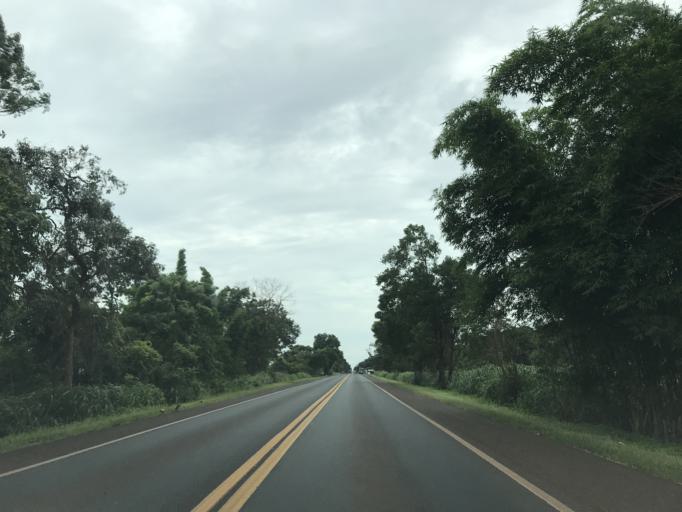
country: BR
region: Minas Gerais
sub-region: Frutal
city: Frutal
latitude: -20.1023
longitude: -49.0912
